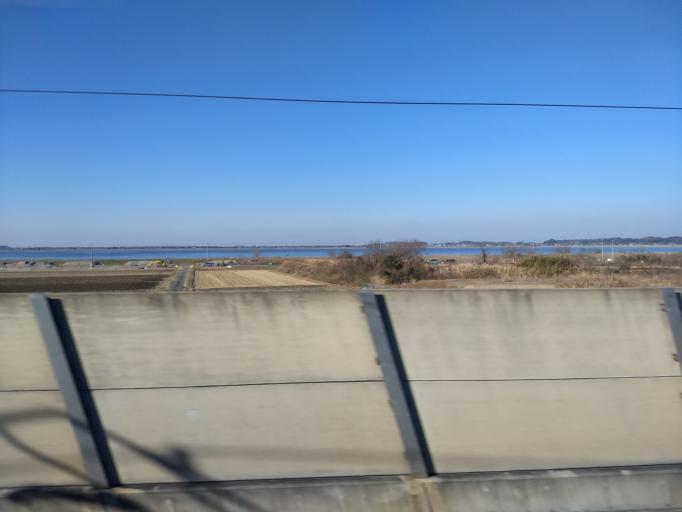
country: JP
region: Chiba
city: Narita
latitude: 35.7924
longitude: 140.2590
